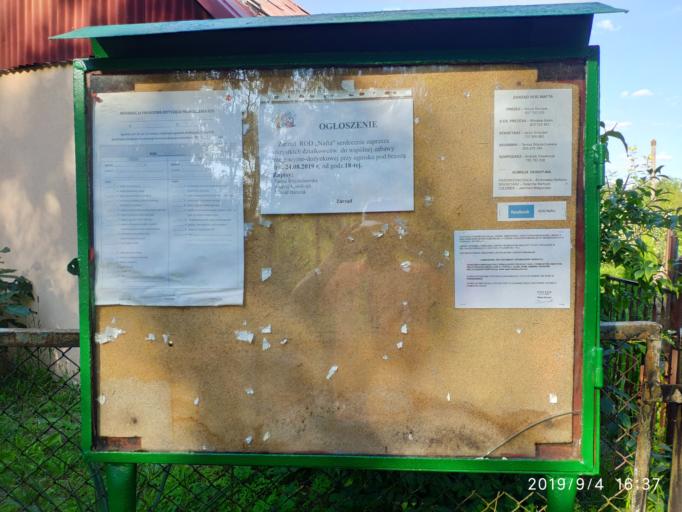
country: PL
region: Lubusz
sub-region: Zielona Gora
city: Zielona Gora
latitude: 51.9129
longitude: 15.5310
